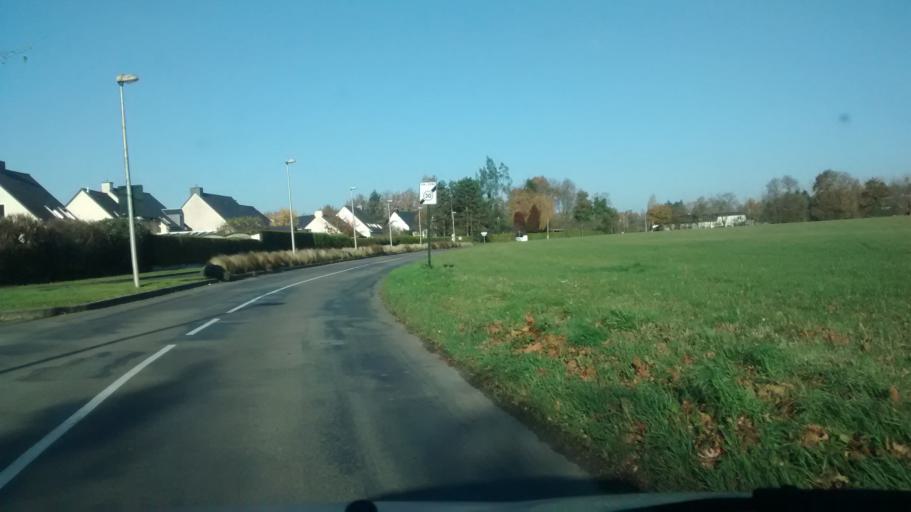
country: FR
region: Brittany
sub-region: Departement d'Ille-et-Vilaine
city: Pace
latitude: 48.1551
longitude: -1.7848
